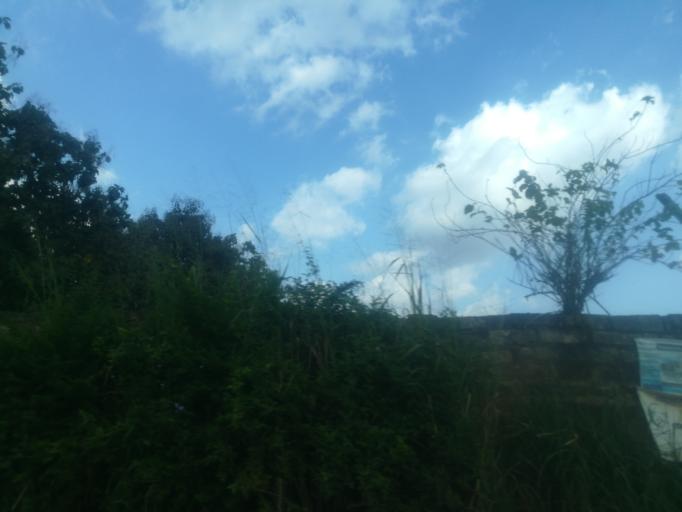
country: NG
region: Oyo
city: Ibadan
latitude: 7.4007
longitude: 3.8409
